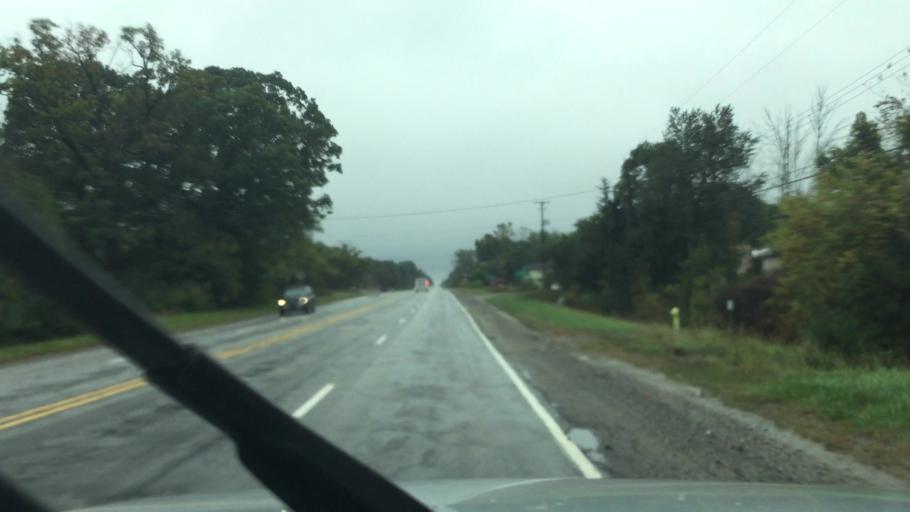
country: US
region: Michigan
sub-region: Saginaw County
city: Bridgeport
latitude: 43.3237
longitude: -83.8250
